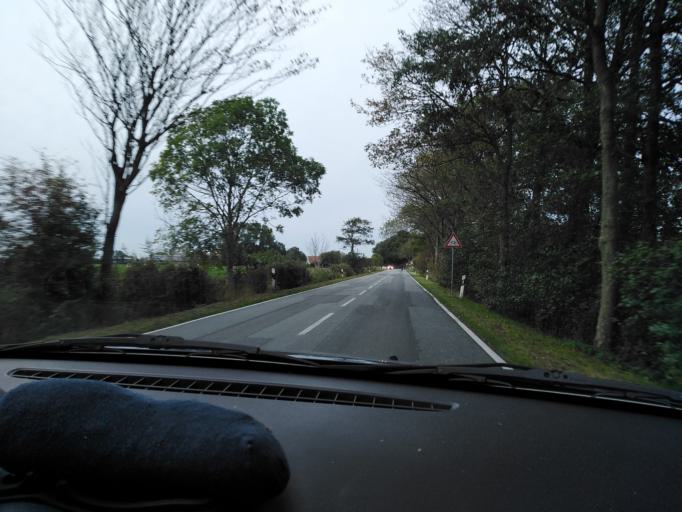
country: DE
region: Lower Saxony
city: Jever
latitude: 53.6761
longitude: 7.8649
